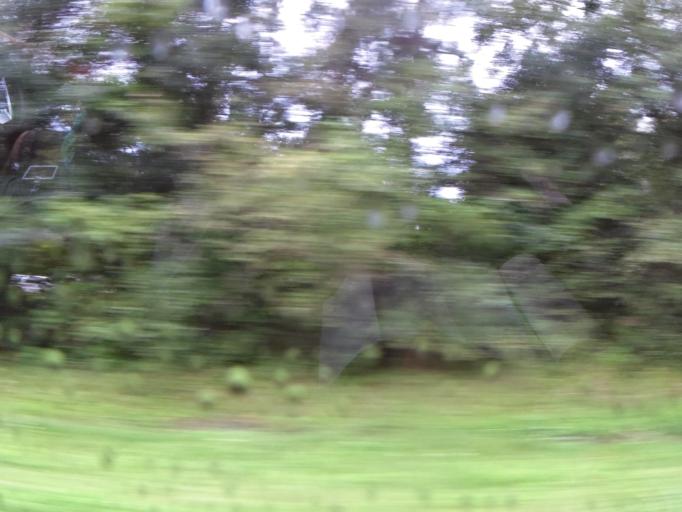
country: US
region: Florida
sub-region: Duval County
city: Baldwin
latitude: 30.4656
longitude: -81.9987
